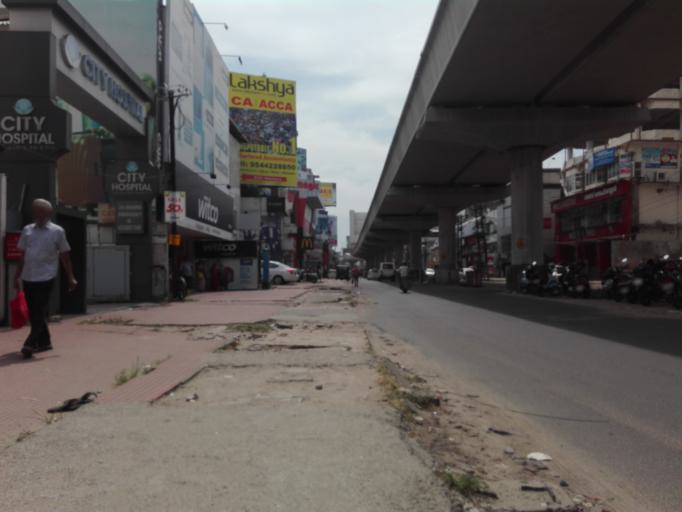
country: IN
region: Kerala
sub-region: Ernakulam
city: Cochin
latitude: 9.9843
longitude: 76.2842
